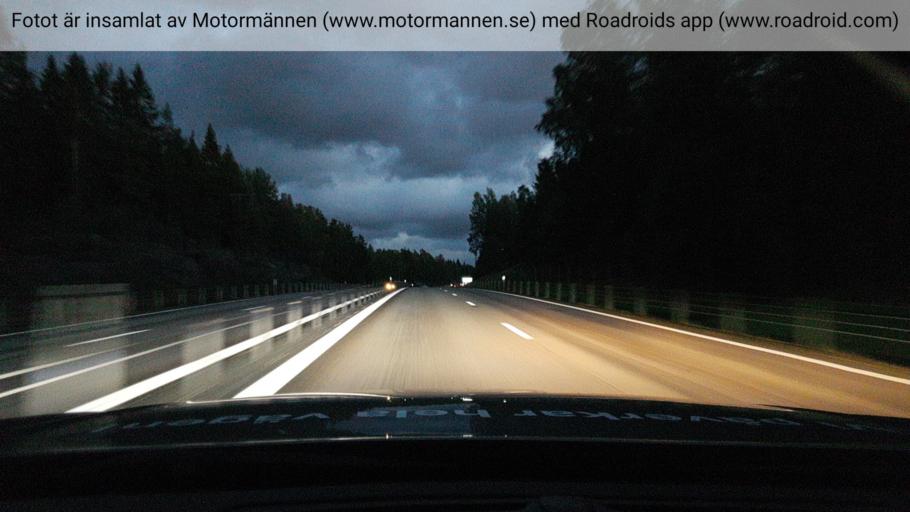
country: SE
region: Vaermland
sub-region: Kristinehamns Kommun
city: Kristinehamn
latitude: 59.3449
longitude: 14.0854
